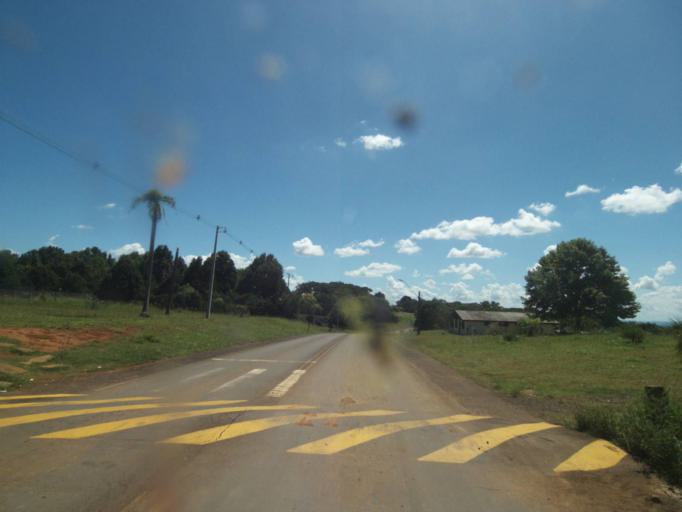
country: BR
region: Parana
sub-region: Pinhao
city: Pinhao
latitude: -25.7915
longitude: -52.0845
